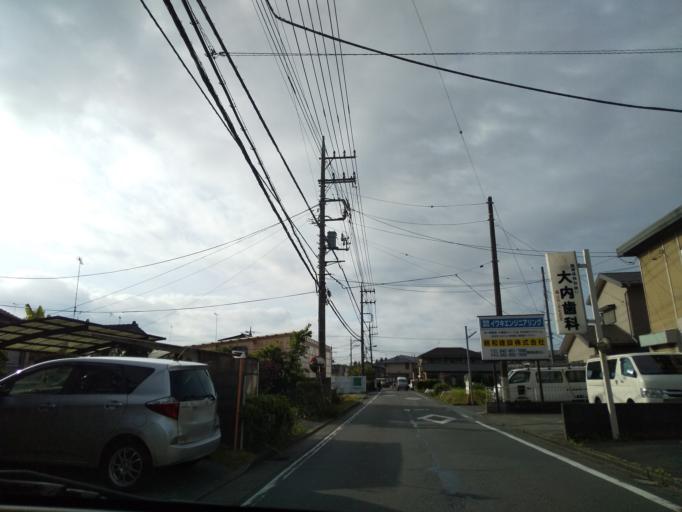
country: JP
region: Tokyo
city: Hachioji
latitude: 35.6867
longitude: 139.3099
